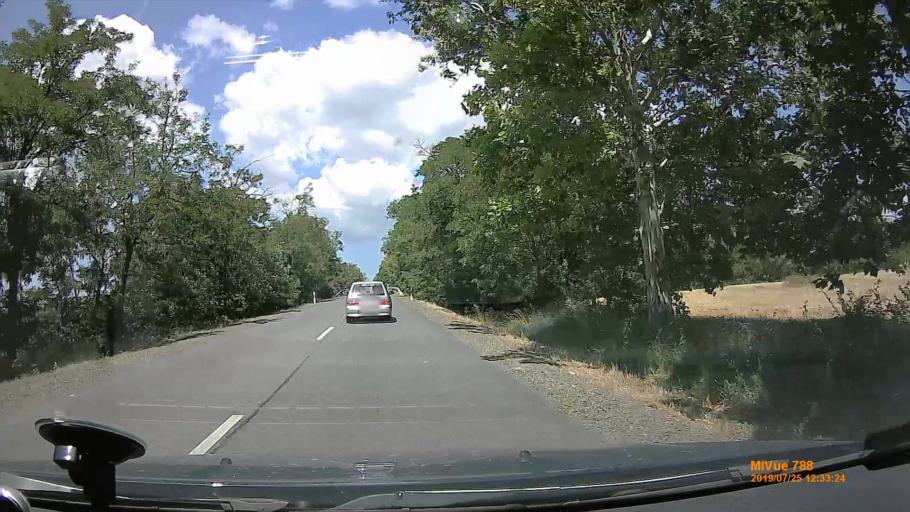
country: HU
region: Borsod-Abauj-Zemplen
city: Mad
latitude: 48.1616
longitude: 21.3075
